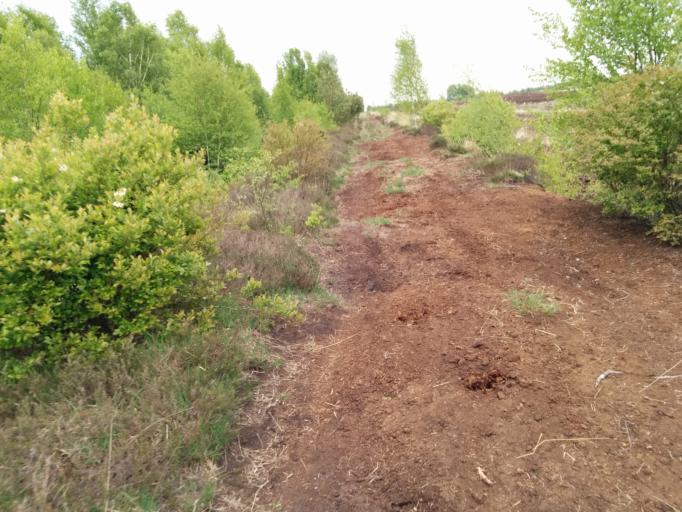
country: DE
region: Lower Saxony
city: Vechta
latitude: 52.7160
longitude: 8.3479
